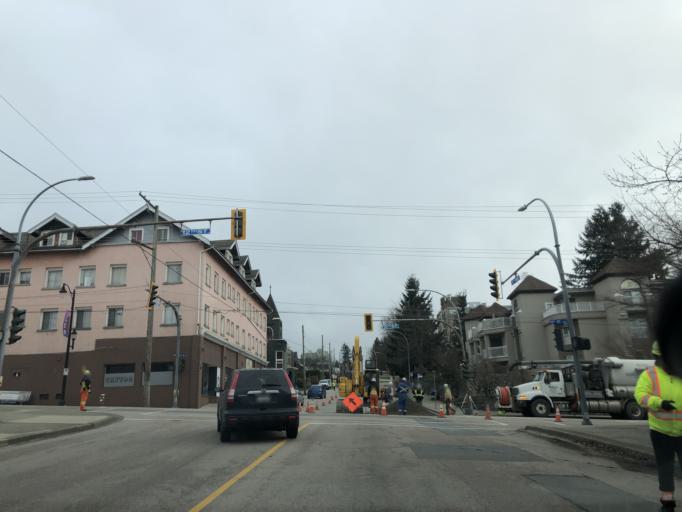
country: CA
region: British Columbia
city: New Westminster
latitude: 49.2074
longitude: -122.9310
